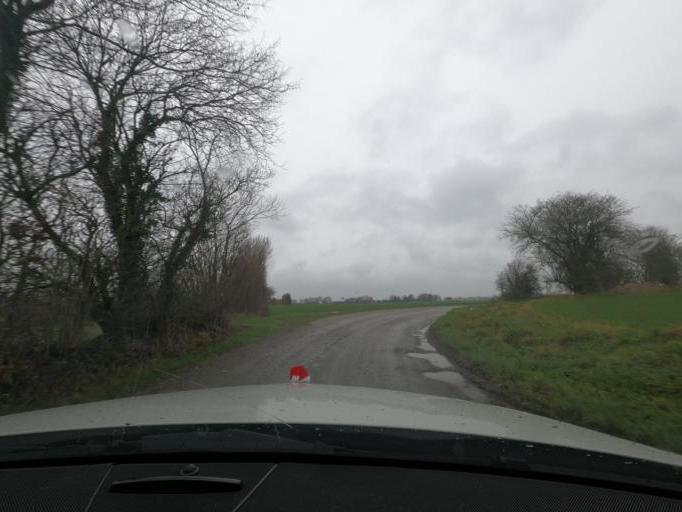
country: DK
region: South Denmark
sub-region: Haderslev Kommune
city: Haderslev
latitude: 55.2272
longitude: 9.5066
